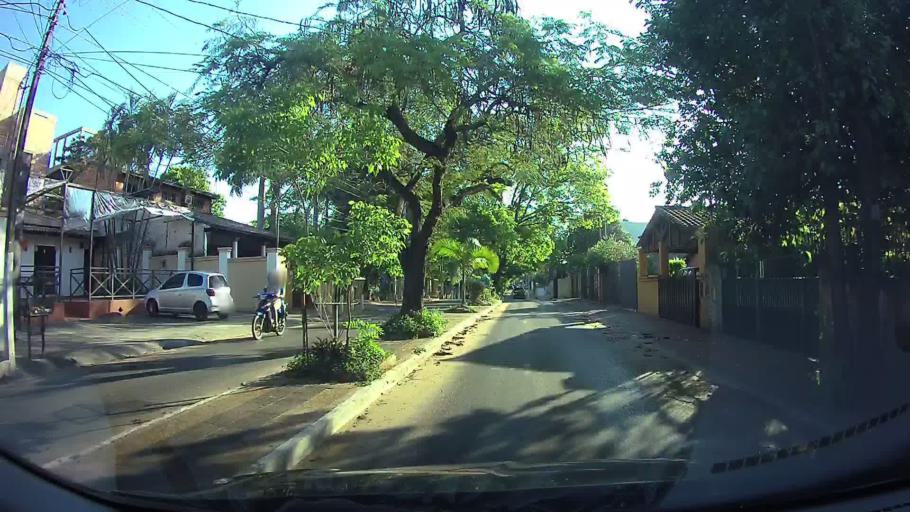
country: PY
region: Central
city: San Lorenzo
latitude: -25.3408
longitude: -57.5048
